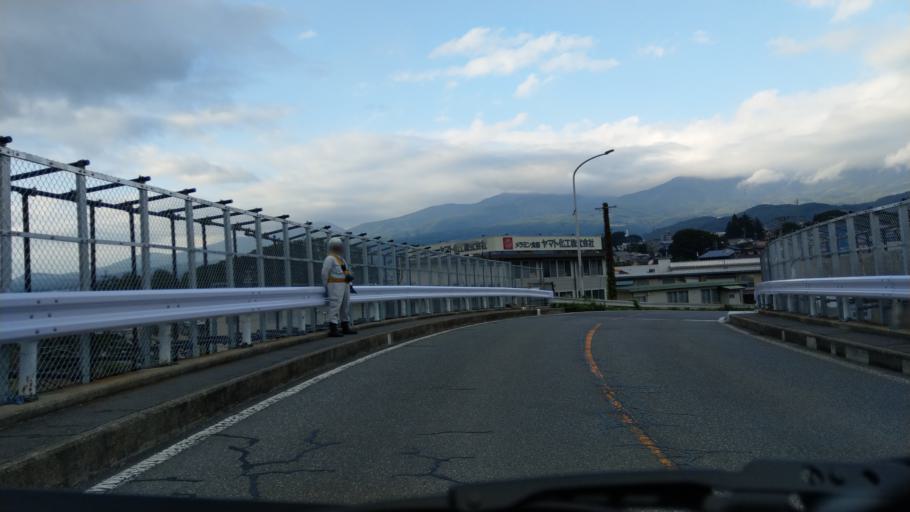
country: JP
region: Nagano
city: Komoro
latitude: 36.3184
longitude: 138.4307
